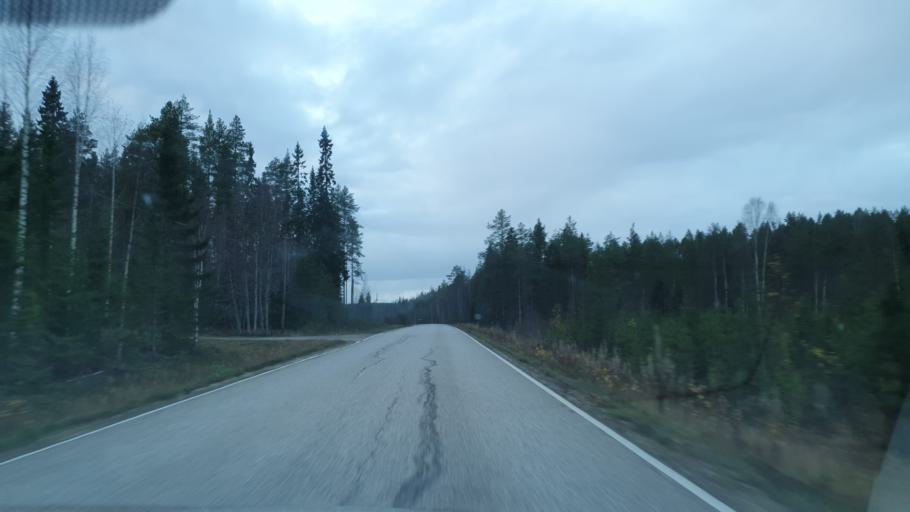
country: FI
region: Kainuu
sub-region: Kajaani
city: Ristijaervi
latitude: 64.4247
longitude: 28.3970
